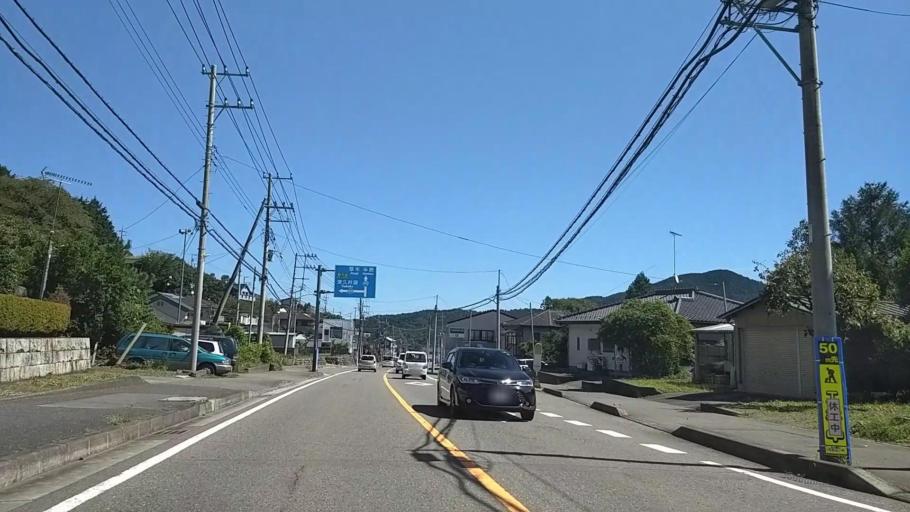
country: JP
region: Tokyo
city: Hachioji
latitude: 35.5663
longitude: 139.2528
